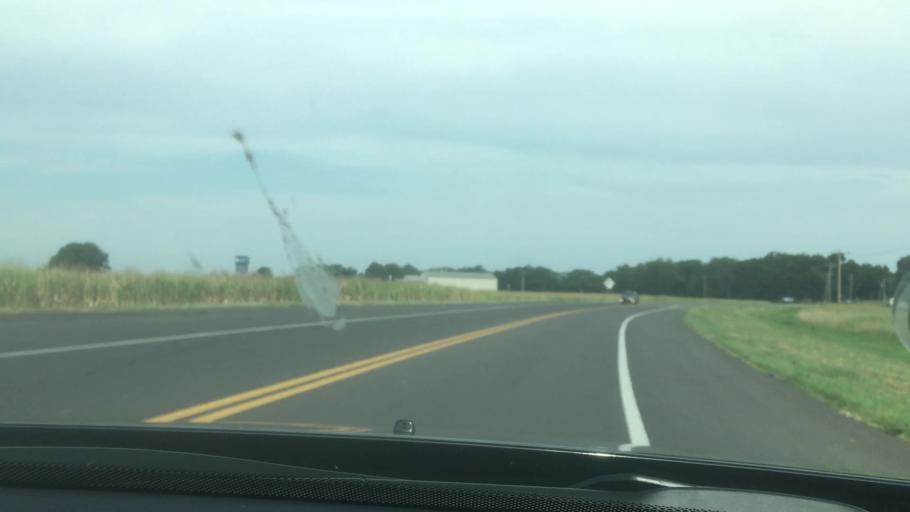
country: US
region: Oklahoma
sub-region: Garvin County
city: Pauls Valley
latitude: 34.7398
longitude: -97.2748
